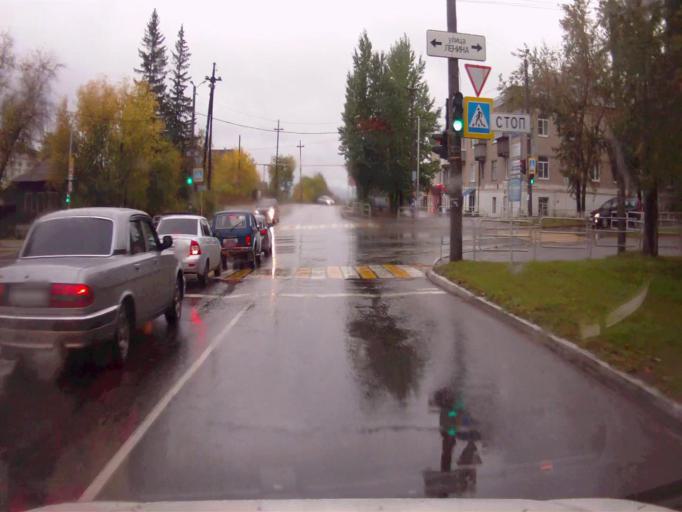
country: RU
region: Chelyabinsk
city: Kyshtym
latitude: 55.7064
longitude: 60.5566
